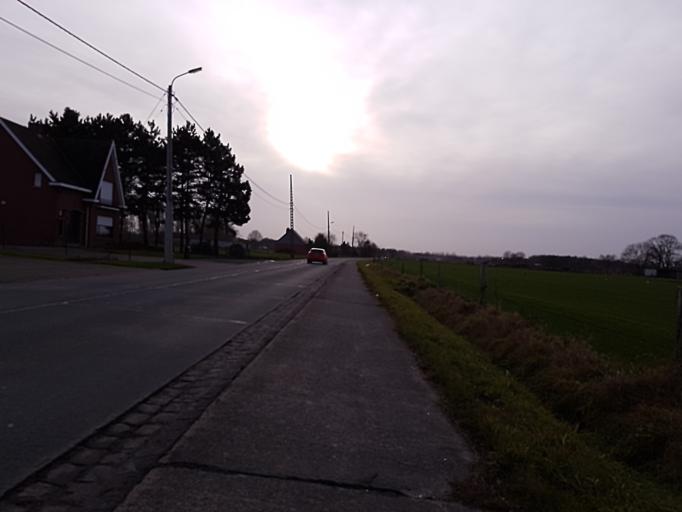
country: BE
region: Flanders
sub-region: Provincie Antwerpen
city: Putte
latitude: 51.0439
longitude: 4.6796
